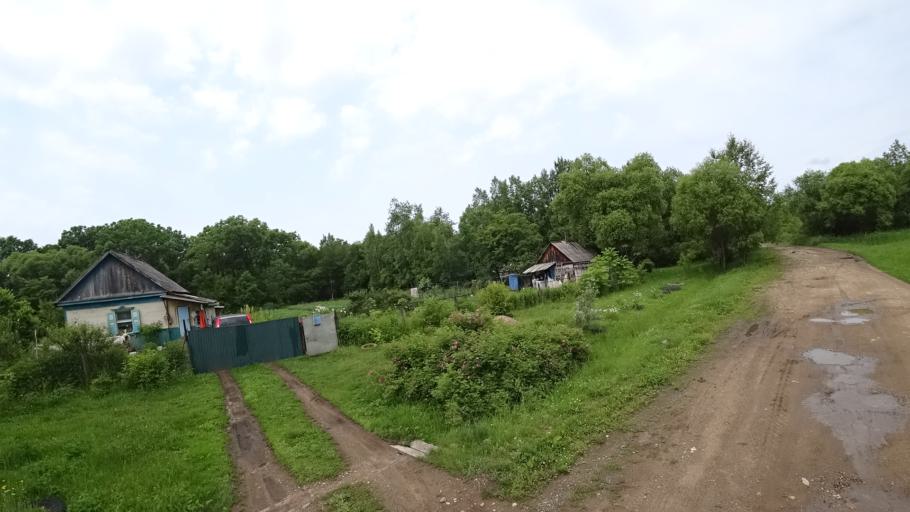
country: RU
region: Primorskiy
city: Novosysoyevka
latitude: 44.2540
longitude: 133.3740
